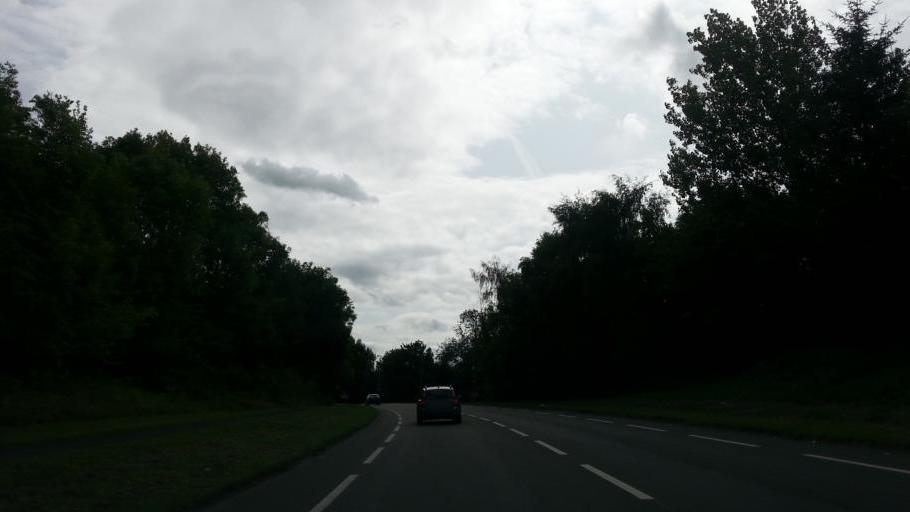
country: GB
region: England
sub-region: Leicestershire
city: Market Harborough
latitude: 52.4883
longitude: -0.9345
